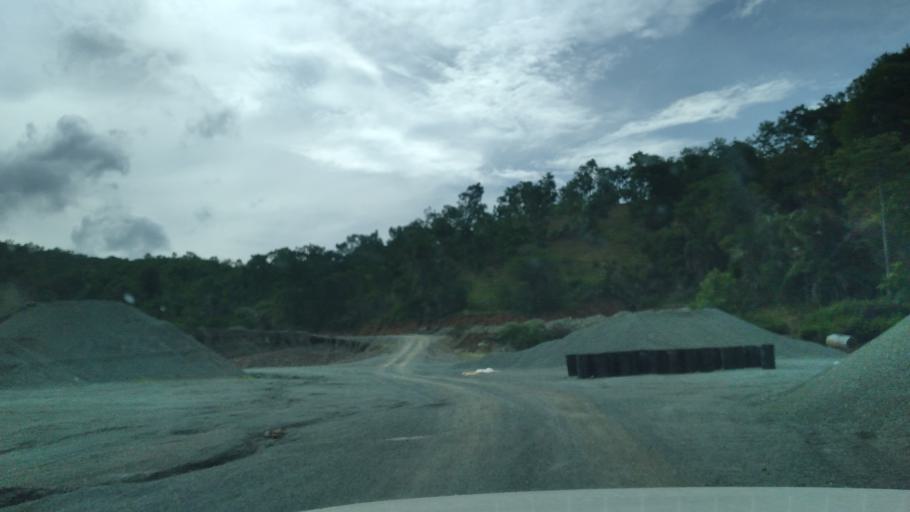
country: TL
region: Dili
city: Dili
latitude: -8.5983
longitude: 125.4786
